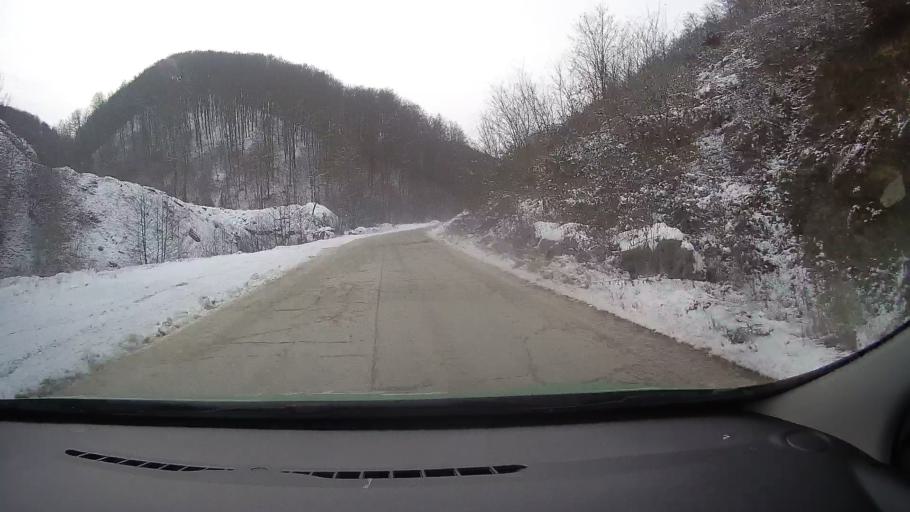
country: RO
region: Alba
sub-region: Oras Zlatna
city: Zlatna
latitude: 46.1001
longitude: 23.1880
